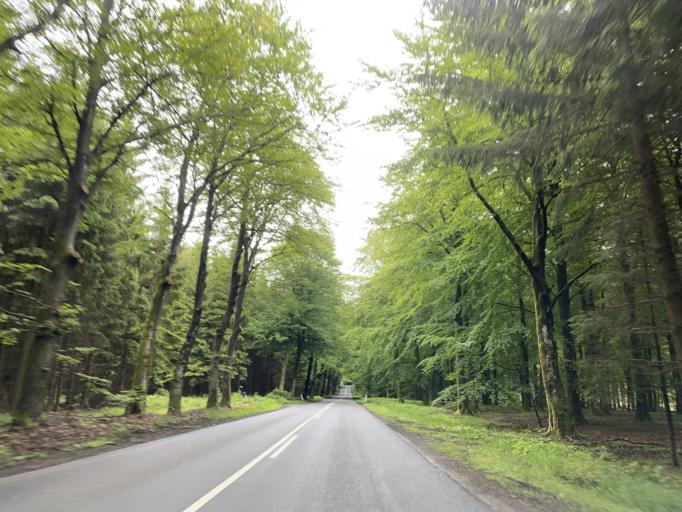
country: DK
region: Central Jutland
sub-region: Favrskov Kommune
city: Hammel
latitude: 56.2594
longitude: 9.9453
